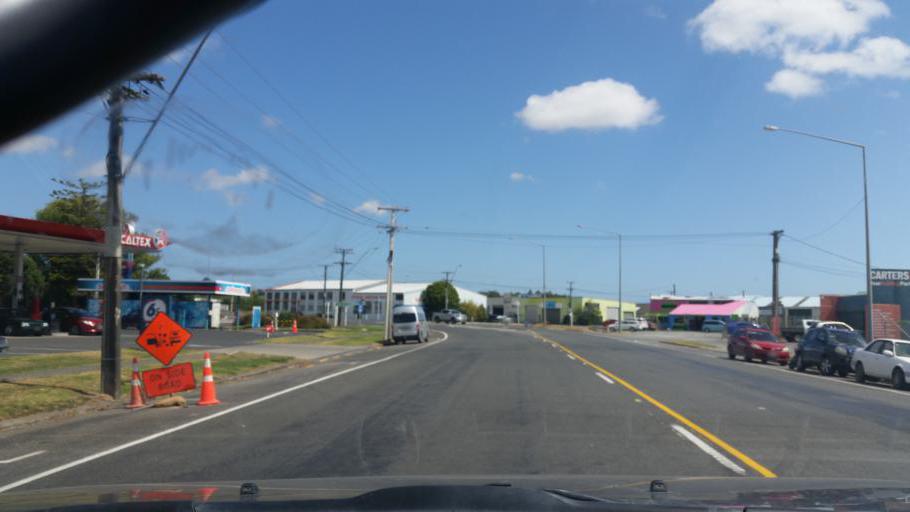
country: NZ
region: Northland
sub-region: Kaipara District
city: Dargaville
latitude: -35.9433
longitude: 173.8666
